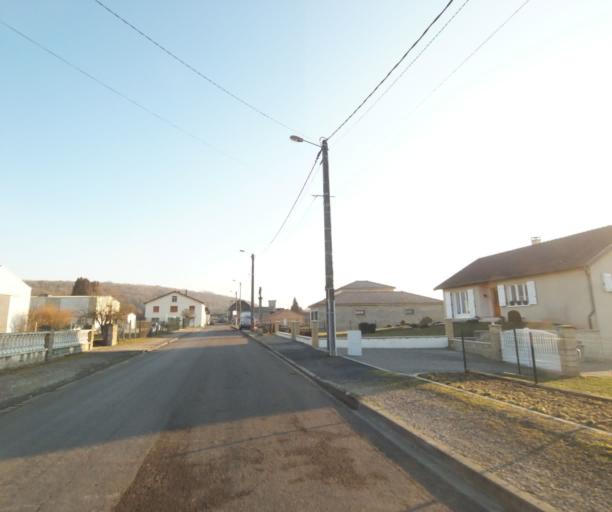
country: FR
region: Champagne-Ardenne
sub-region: Departement de la Haute-Marne
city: Chevillon
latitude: 48.5417
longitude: 5.1024
